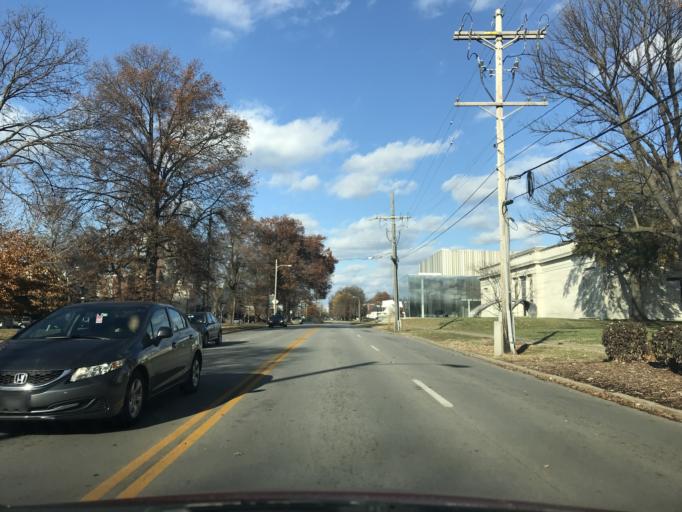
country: US
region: Kentucky
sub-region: Jefferson County
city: Louisville
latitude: 38.2168
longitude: -85.7618
